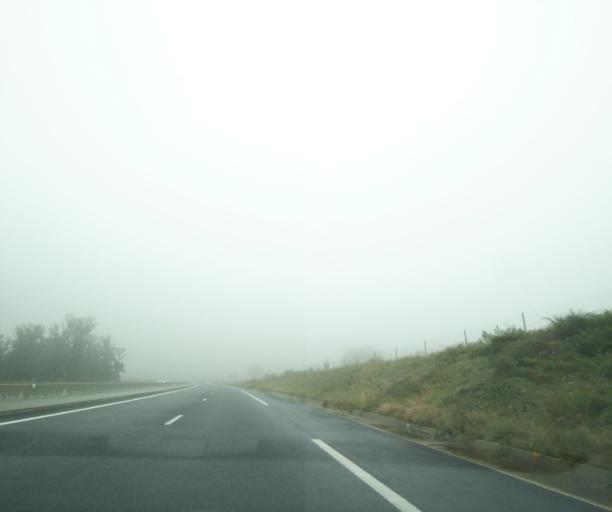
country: FR
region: Midi-Pyrenees
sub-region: Departement de l'Aveyron
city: Naucelle
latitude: 44.1773
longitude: 2.3576
